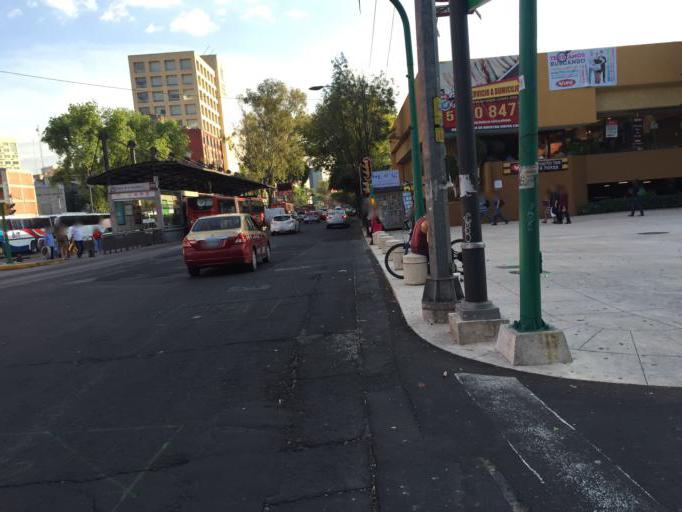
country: MX
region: Mexico City
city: Cuauhtemoc
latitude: 19.4367
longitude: -99.1572
